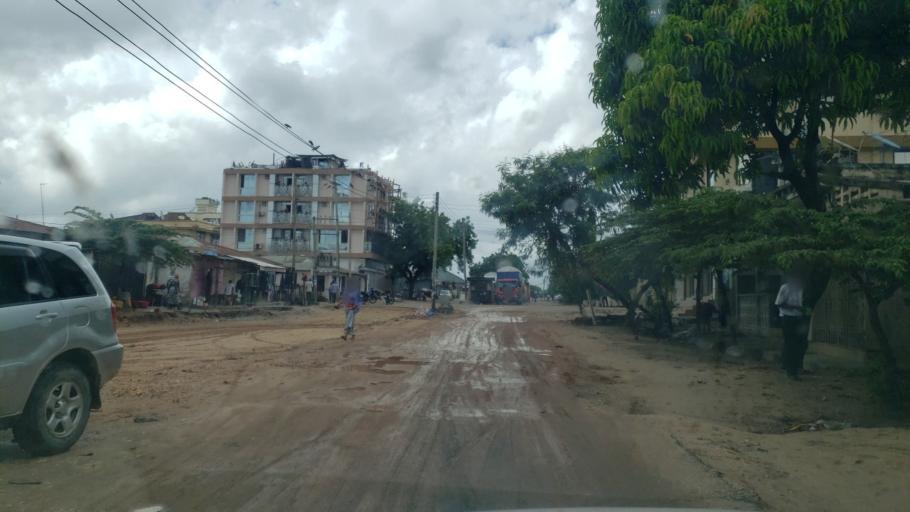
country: TZ
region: Dar es Salaam
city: Magomeni
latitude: -6.8112
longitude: 39.2592
